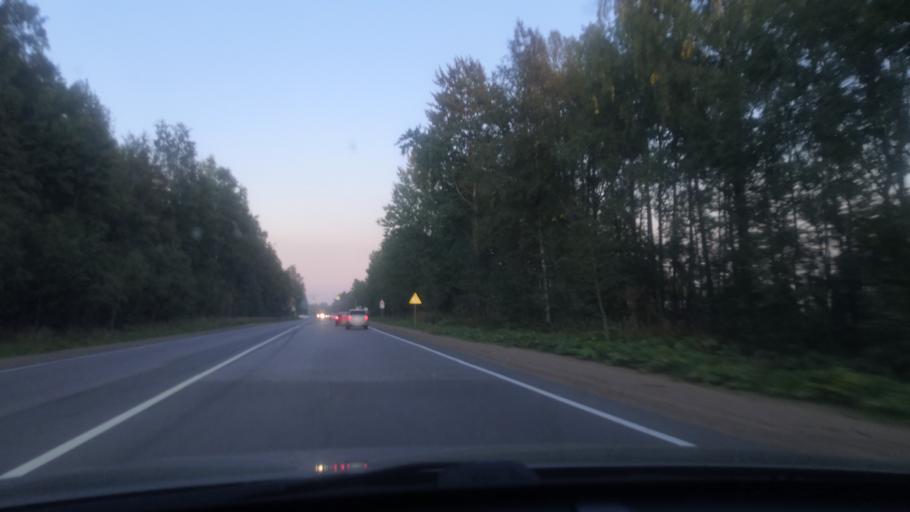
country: RU
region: St.-Petersburg
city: Beloostrov
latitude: 60.1985
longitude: 30.0024
